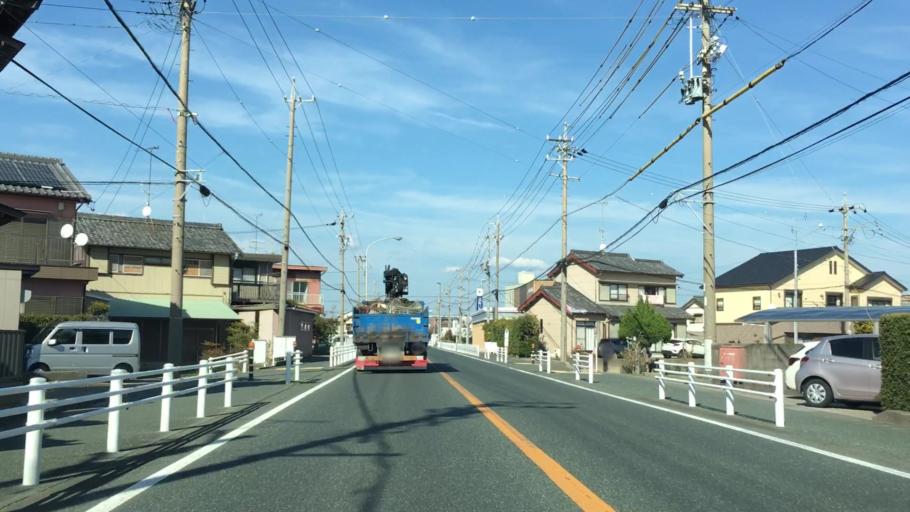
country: JP
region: Shizuoka
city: Kosai-shi
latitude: 34.6896
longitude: 137.5630
